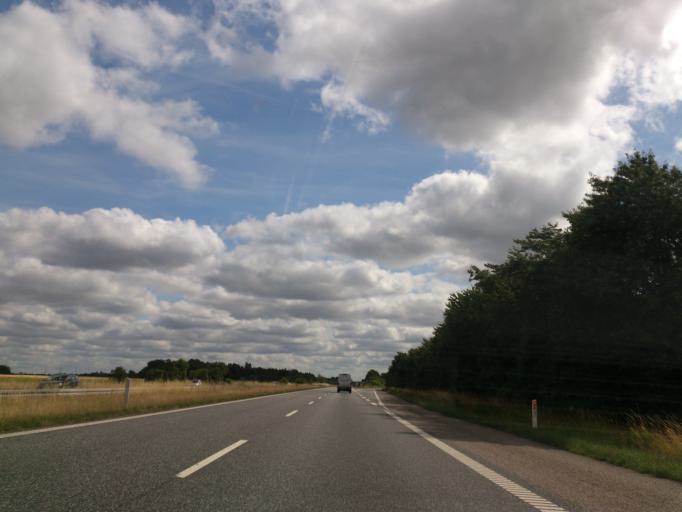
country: DK
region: South Denmark
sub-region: Aabenraa Kommune
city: Krusa
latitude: 54.9210
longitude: 9.3829
